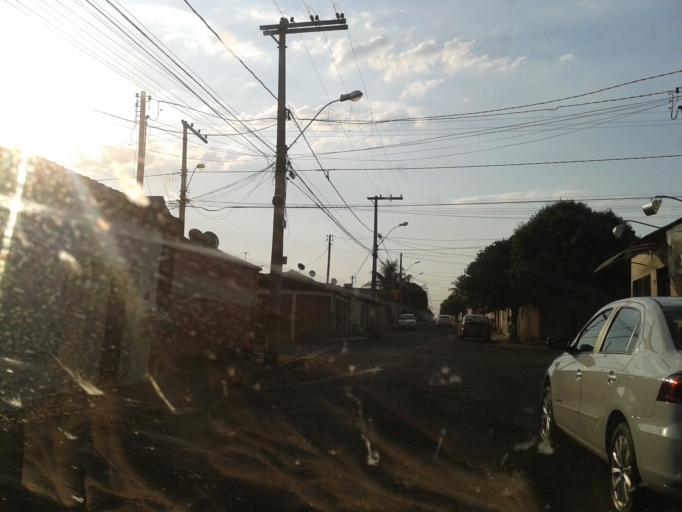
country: BR
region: Minas Gerais
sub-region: Uberlandia
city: Uberlandia
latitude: -18.9166
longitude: -48.3307
